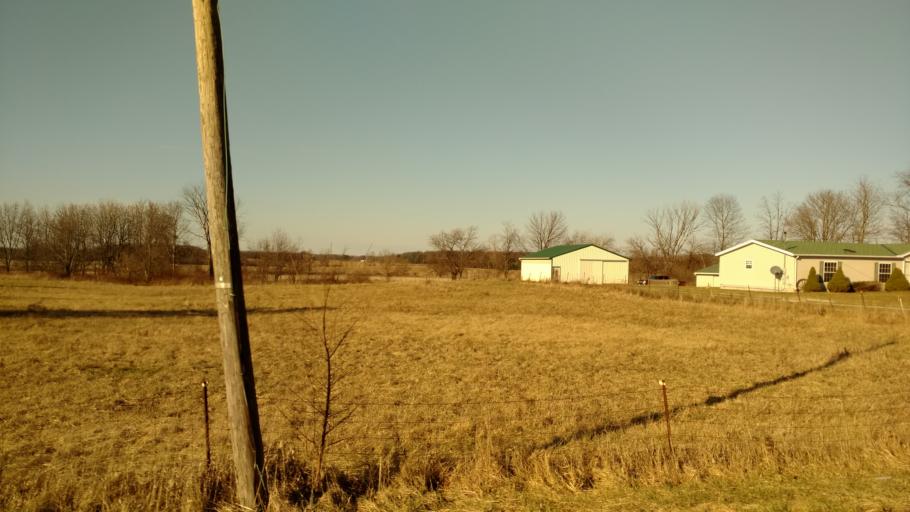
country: US
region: Ohio
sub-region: Crawford County
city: Galion
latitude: 40.7112
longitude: -82.7249
